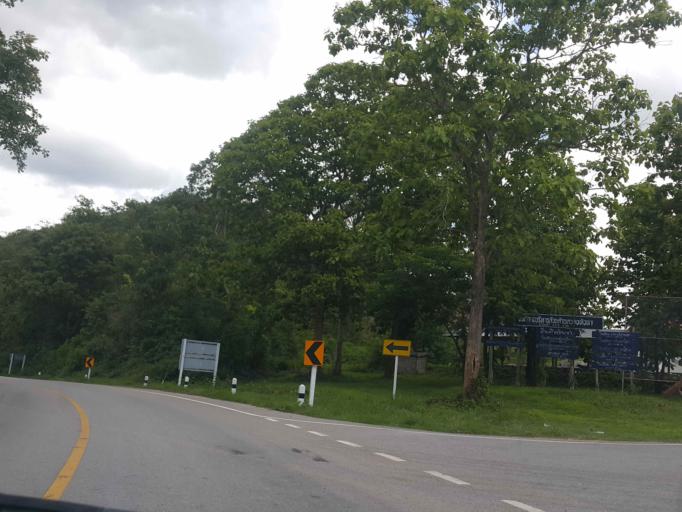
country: TH
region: Nan
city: Wiang Sa
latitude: 18.5238
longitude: 100.5555
